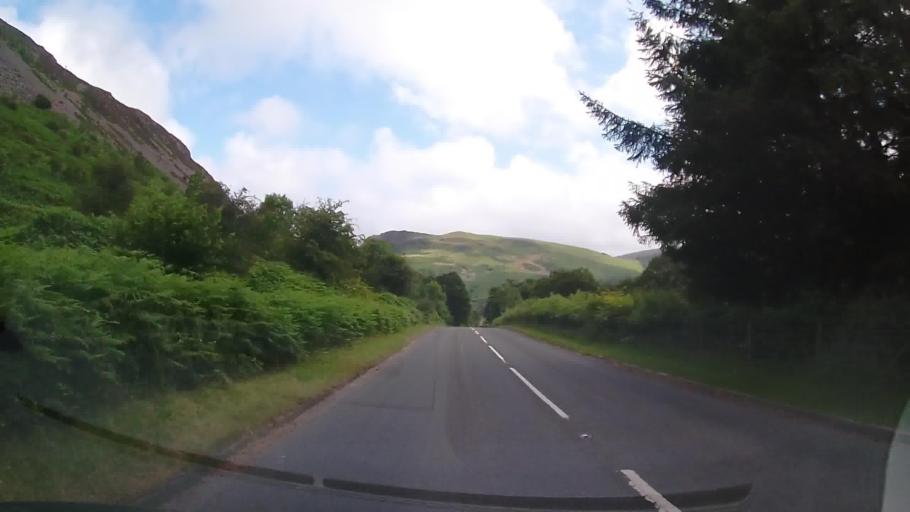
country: GB
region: Wales
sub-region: Sir Powys
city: Llangynog
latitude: 52.8314
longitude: -3.4147
